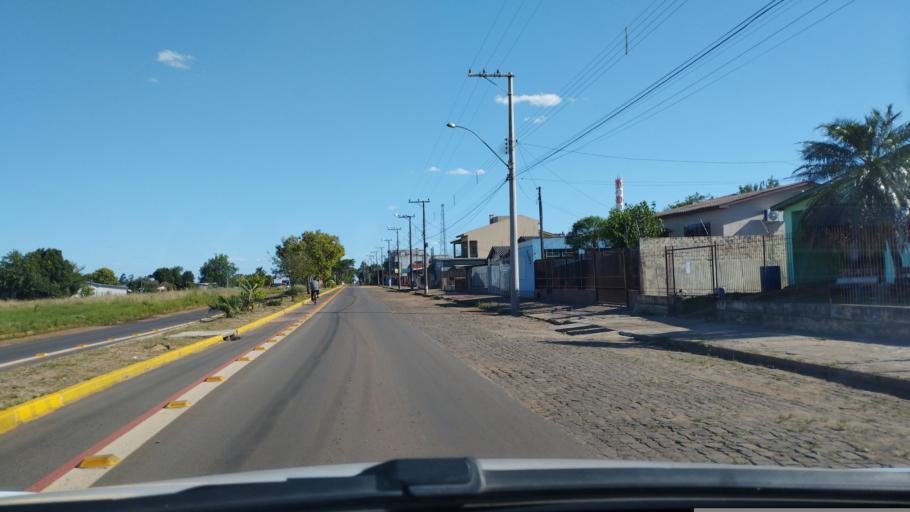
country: BR
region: Rio Grande do Sul
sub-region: Tupancireta
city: Tupancireta
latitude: -29.0773
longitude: -53.8364
